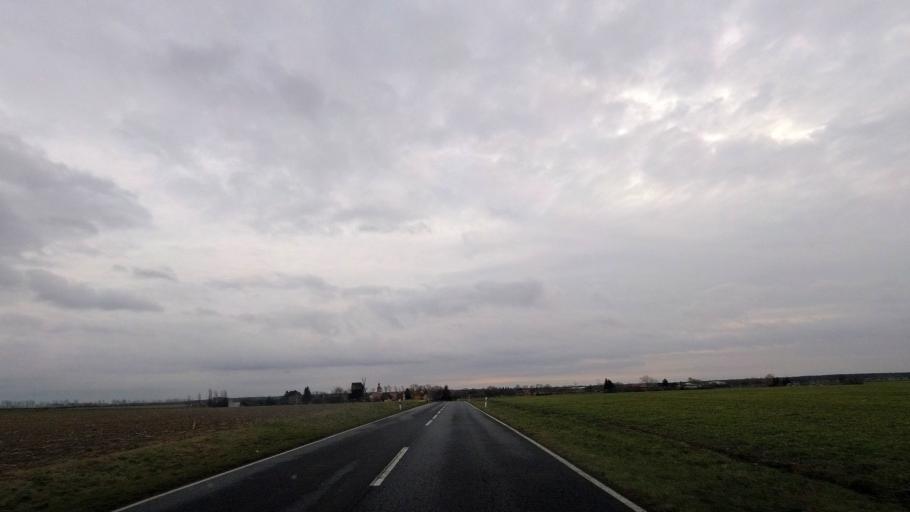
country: DE
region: Brandenburg
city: Niedergorsdorf
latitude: 51.9626
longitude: 12.9800
